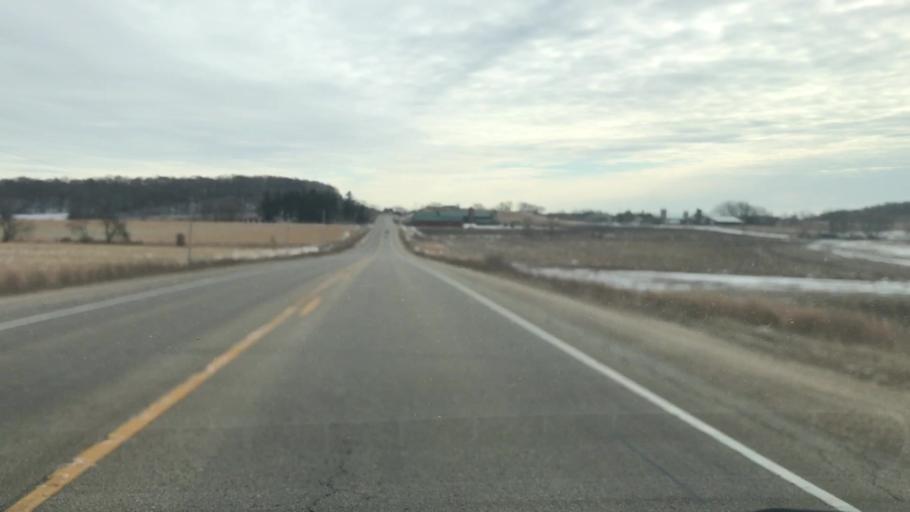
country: US
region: Wisconsin
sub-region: Dodge County
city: Theresa
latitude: 43.4352
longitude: -88.4685
